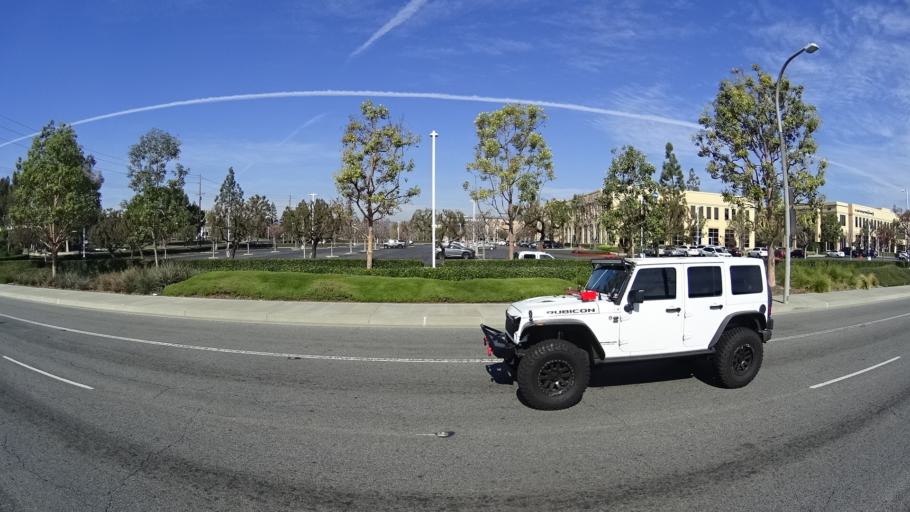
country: US
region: California
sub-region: Orange County
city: Brea
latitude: 33.9174
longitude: -117.9148
